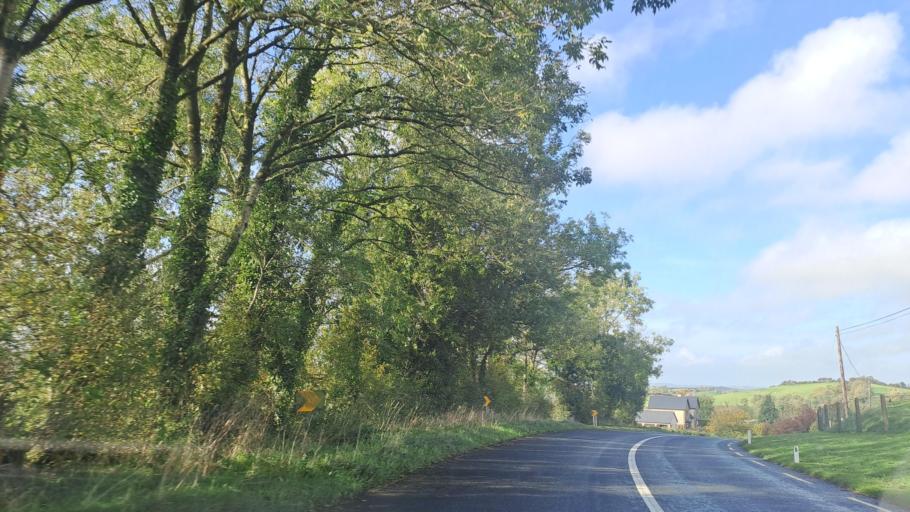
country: IE
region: Ulster
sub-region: An Cabhan
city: Cootehill
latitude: 54.0587
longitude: -7.0295
